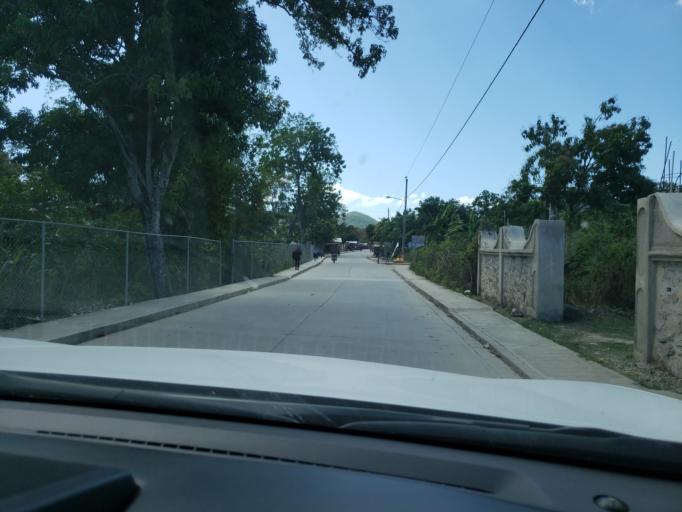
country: HT
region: Grandans
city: Anse-a-Veau
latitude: 18.4493
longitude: -73.3857
